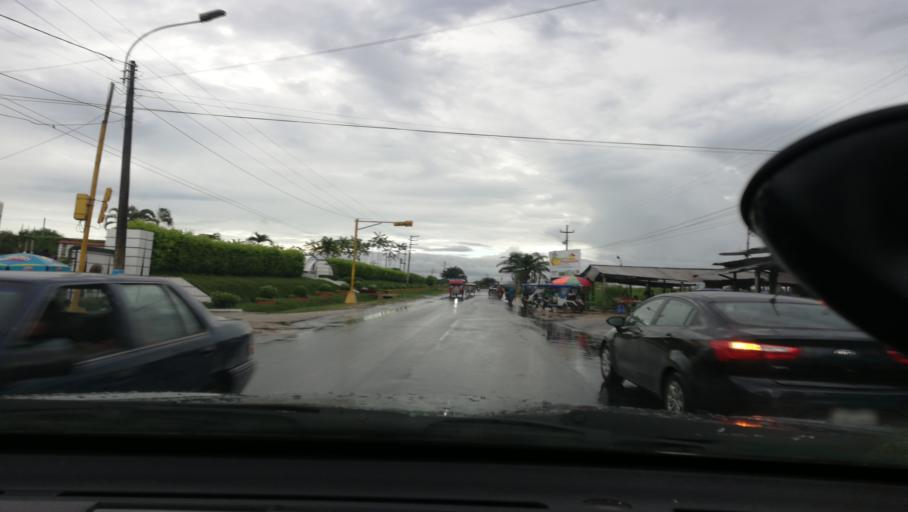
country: PE
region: Loreto
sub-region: Provincia de Maynas
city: Iquitos
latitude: -3.8462
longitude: -73.3368
